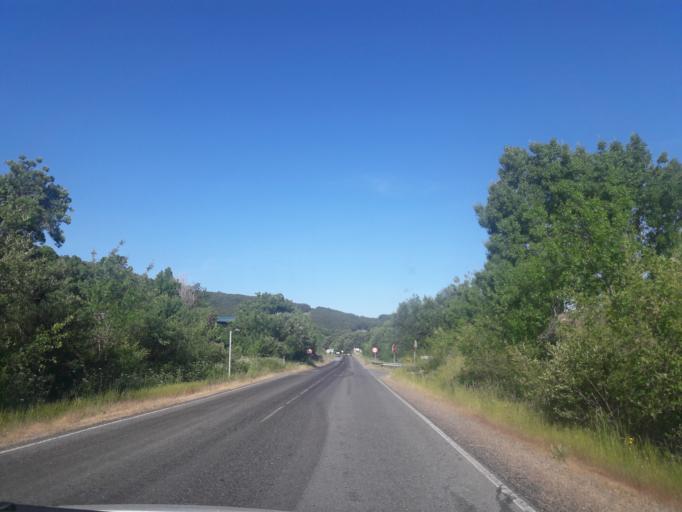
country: ES
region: Castille and Leon
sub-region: Provincia de Salamanca
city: Penacaballera
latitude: 40.3434
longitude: -5.8662
